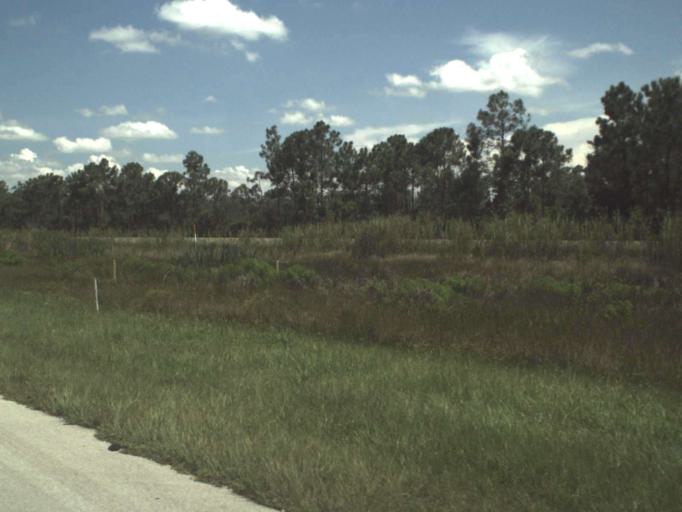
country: US
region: Florida
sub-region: Martin County
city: Indiantown
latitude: 26.9342
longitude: -80.3387
